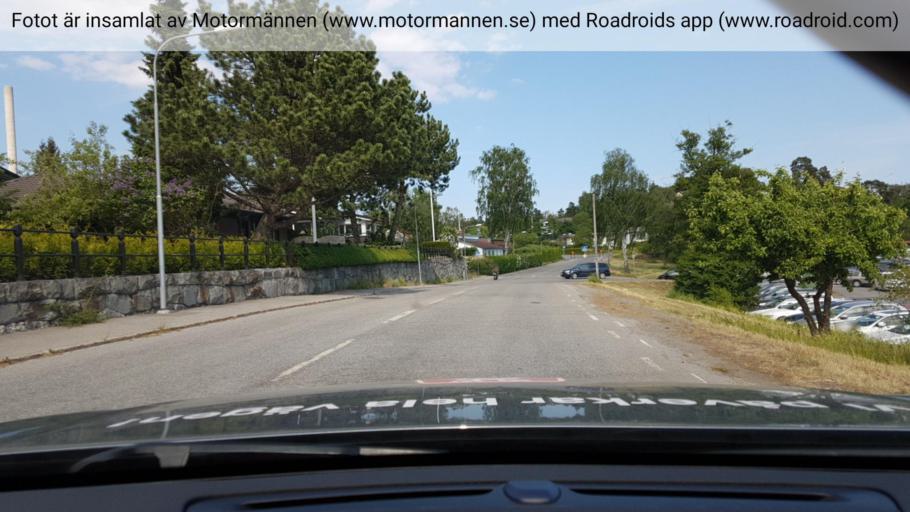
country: SE
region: Stockholm
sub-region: Lidingo
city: Brevik
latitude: 59.3491
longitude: 18.2238
